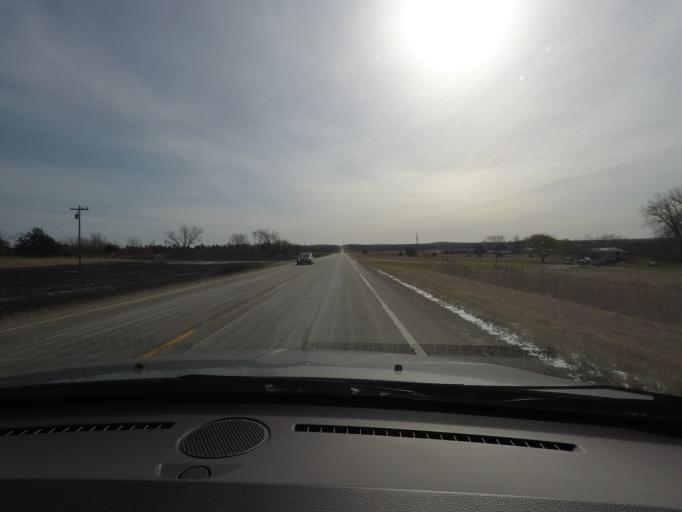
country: US
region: Kansas
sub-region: Morris County
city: Council Grove
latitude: 38.6667
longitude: -96.3762
